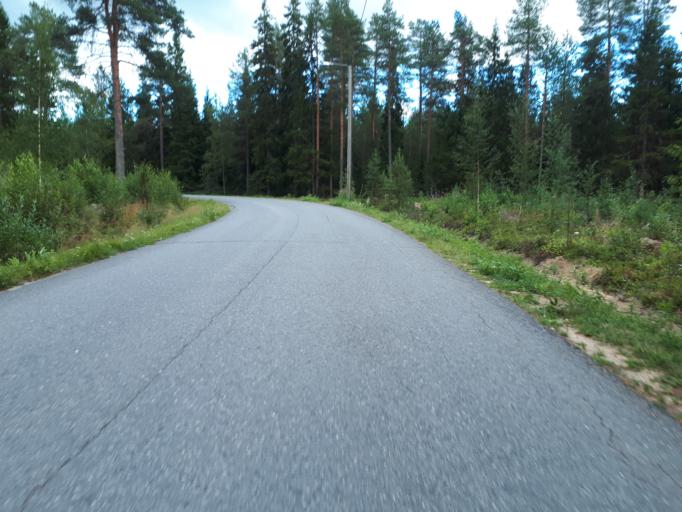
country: FI
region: Northern Ostrobothnia
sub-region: Oulunkaari
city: Ii
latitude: 65.3257
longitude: 25.3929
